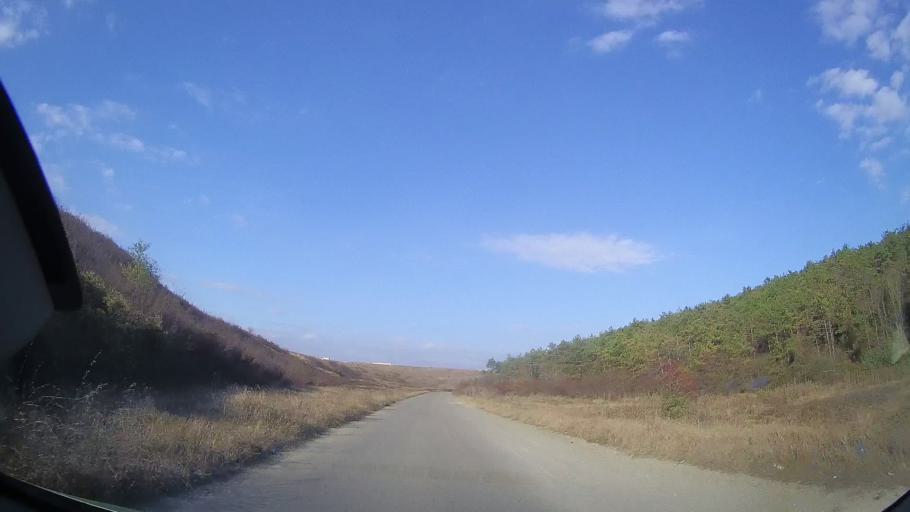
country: RO
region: Constanta
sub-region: Comuna Limanu
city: Limanu
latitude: 43.8163
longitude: 28.5176
